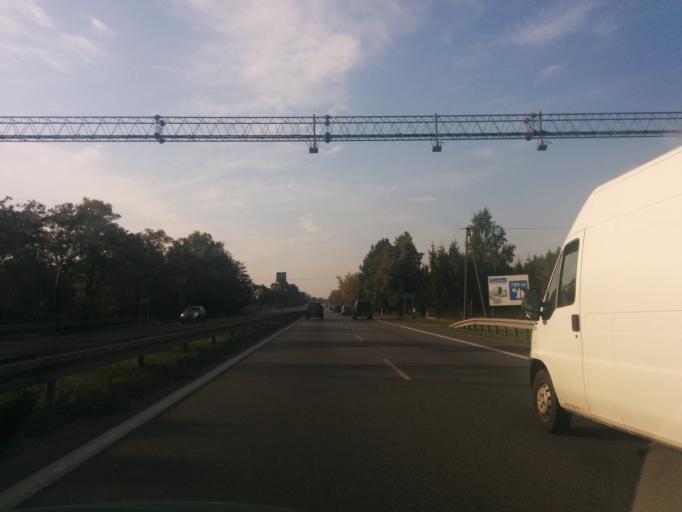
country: PL
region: Masovian Voivodeship
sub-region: Powiat piaseczynski
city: Tarczyn
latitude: 52.0365
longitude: 20.8603
